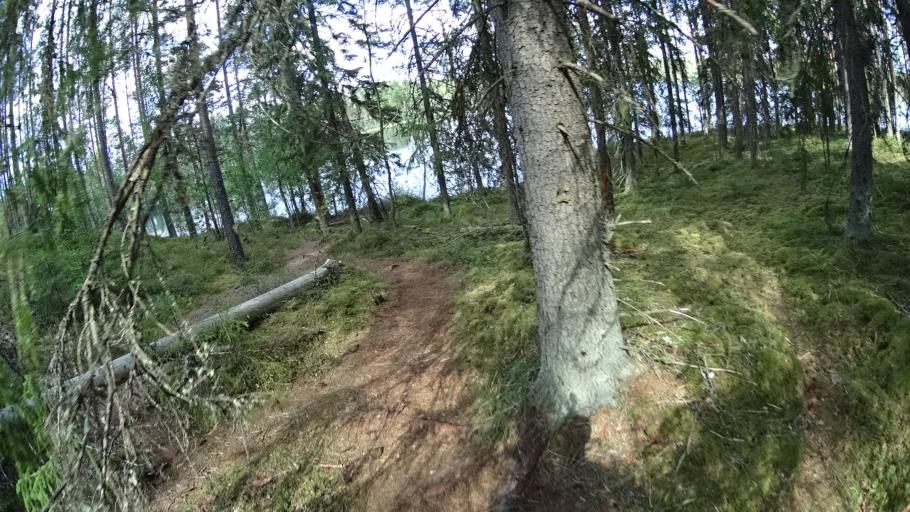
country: FI
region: Uusimaa
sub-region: Helsinki
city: Kaerkoelae
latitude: 60.7347
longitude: 24.0738
